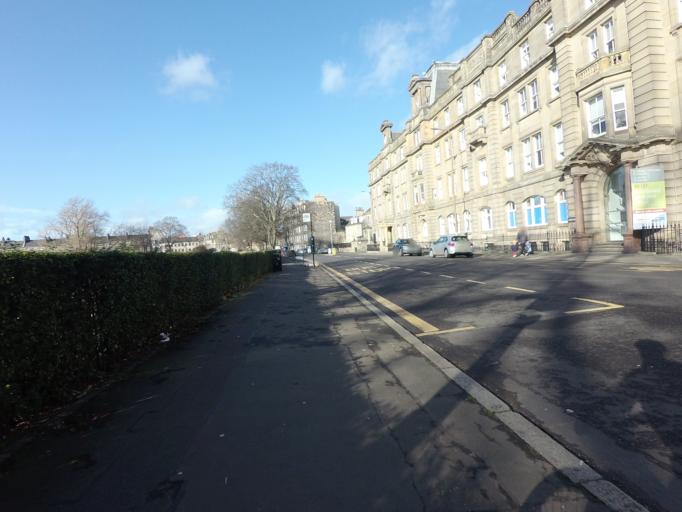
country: GB
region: Scotland
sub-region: West Lothian
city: Seafield
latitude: 55.9723
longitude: -3.1630
